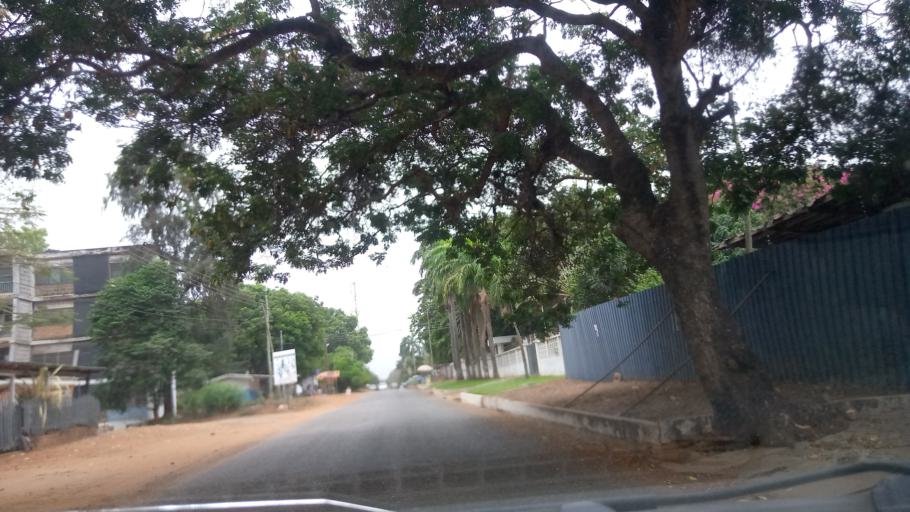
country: GH
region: Greater Accra
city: Accra
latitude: 5.6062
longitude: -0.1875
